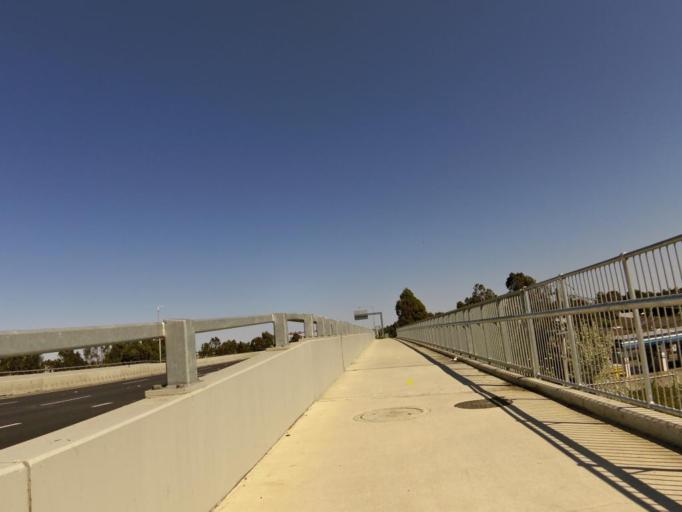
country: AU
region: Victoria
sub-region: Whittlesea
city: Thomastown
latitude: -37.6857
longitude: 145.0135
